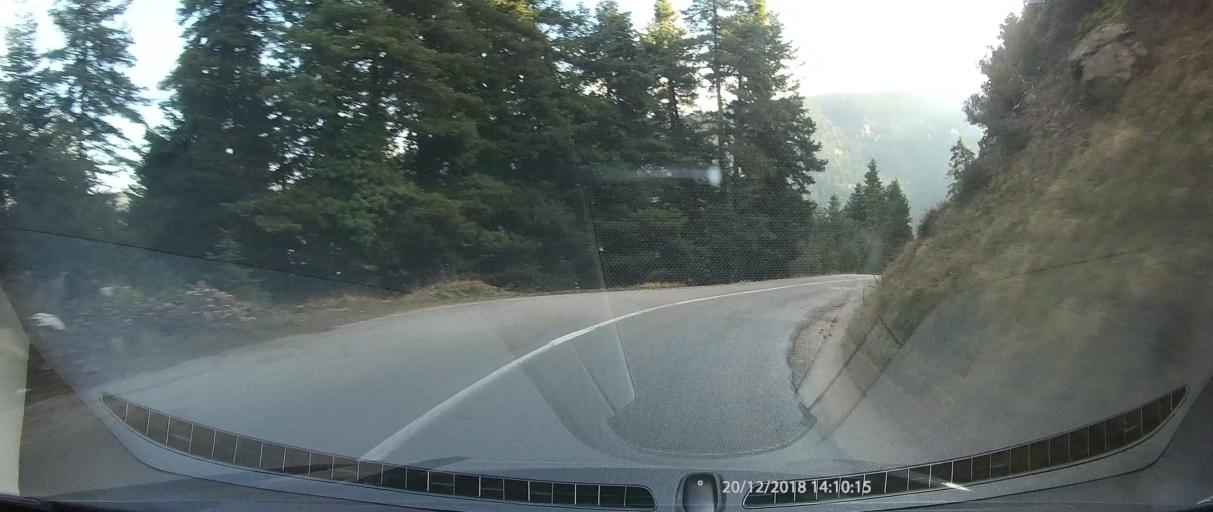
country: GR
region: West Greece
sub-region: Nomos Aitolias kai Akarnanias
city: Thermo
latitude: 38.7470
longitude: 21.6489
